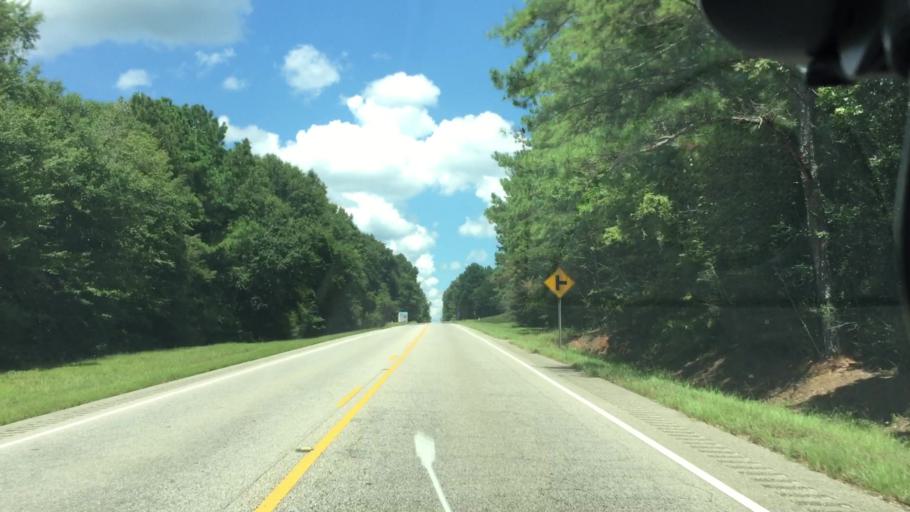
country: US
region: Alabama
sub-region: Coffee County
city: New Brockton
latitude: 31.4469
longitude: -85.8944
